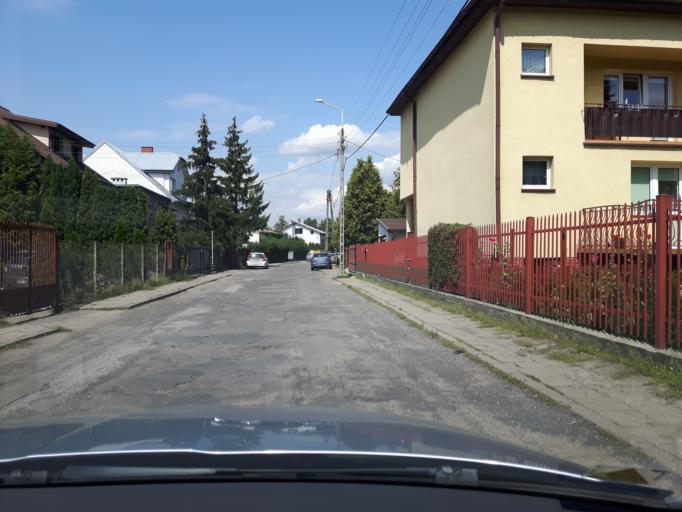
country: PL
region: Masovian Voivodeship
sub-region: Powiat wolominski
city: Zabki
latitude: 52.2913
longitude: 21.1272
